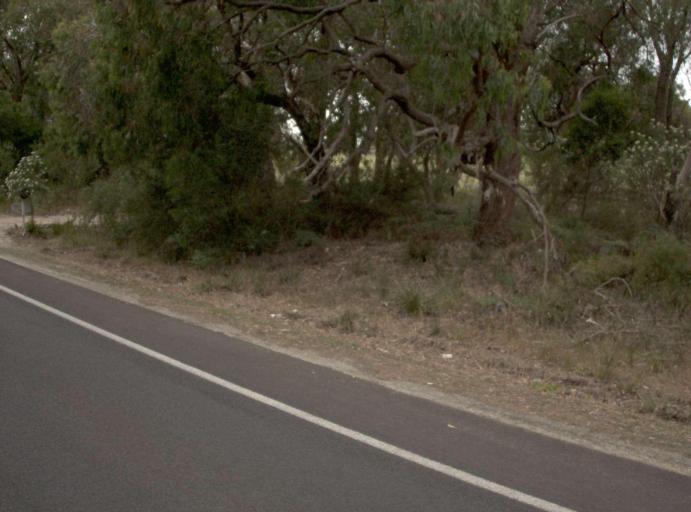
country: AU
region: Victoria
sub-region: Wellington
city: Sale
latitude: -38.1883
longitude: 147.0803
